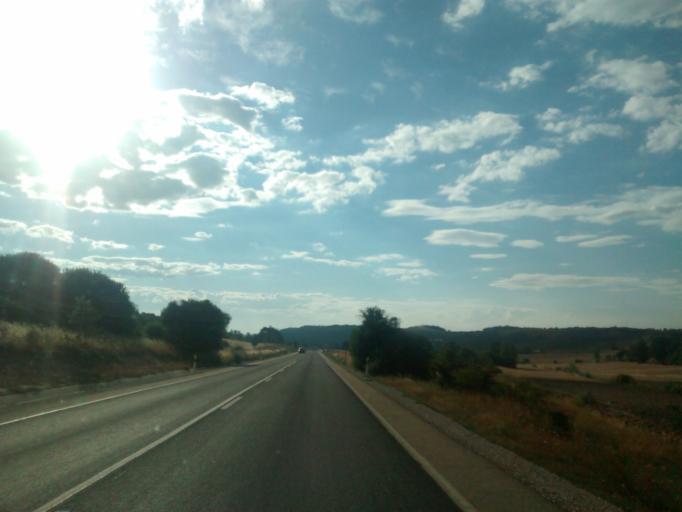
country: ES
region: Castille and Leon
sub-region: Provincia de Burgos
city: Basconcillos del Tozo
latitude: 42.6720
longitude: -3.9313
